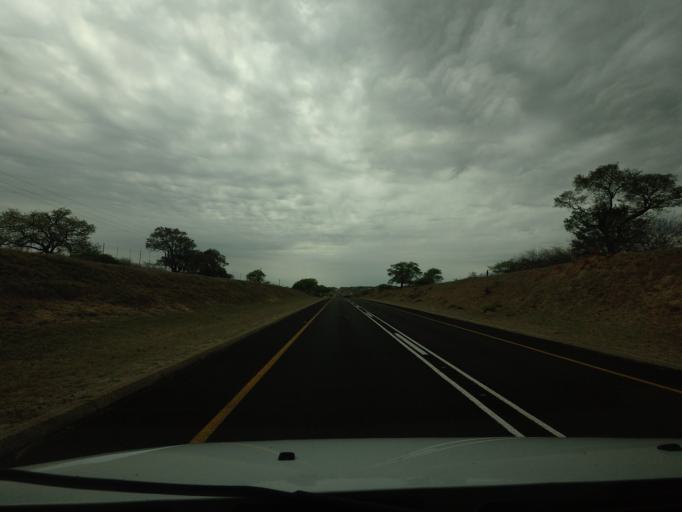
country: ZA
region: Limpopo
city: Thulamahashi
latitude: -24.5641
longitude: 31.1302
